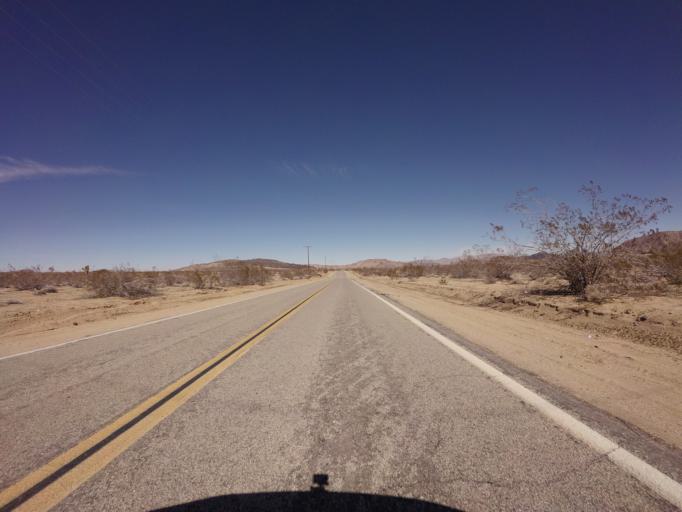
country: US
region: California
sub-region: San Bernardino County
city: Yucca Valley
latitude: 34.2790
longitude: -116.4044
